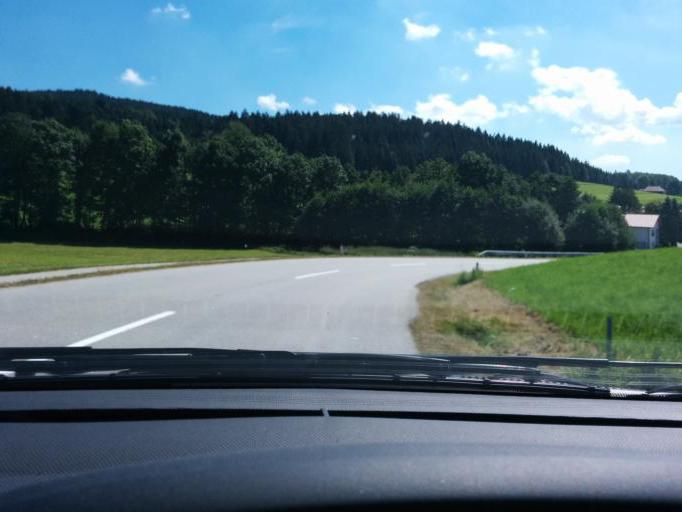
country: AT
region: Upper Austria
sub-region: Politischer Bezirk Rohrbach
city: Ulrichsberg
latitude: 48.7059
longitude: 13.9046
